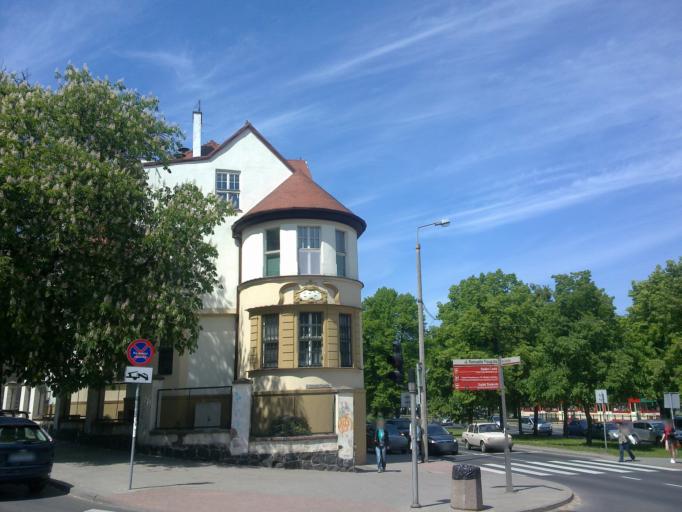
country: PL
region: Pomeranian Voivodeship
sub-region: Gdansk
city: Gdansk
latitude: 54.3685
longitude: 18.6298
